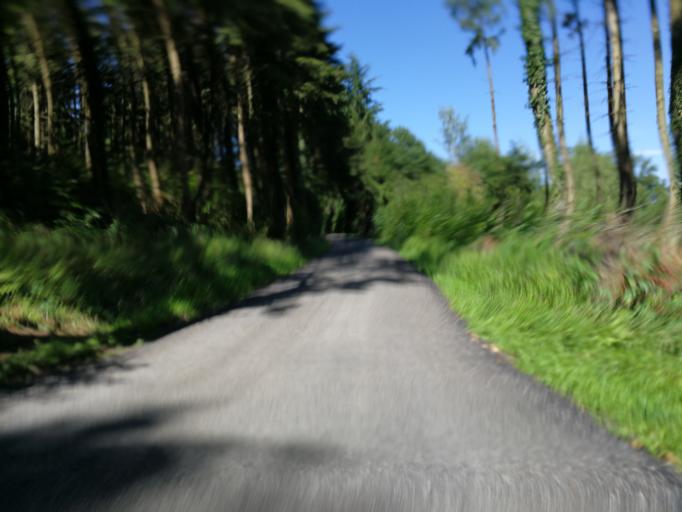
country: CH
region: Zurich
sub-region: Bezirk Hinwil
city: Gossau
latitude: 47.3166
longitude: 8.7542
